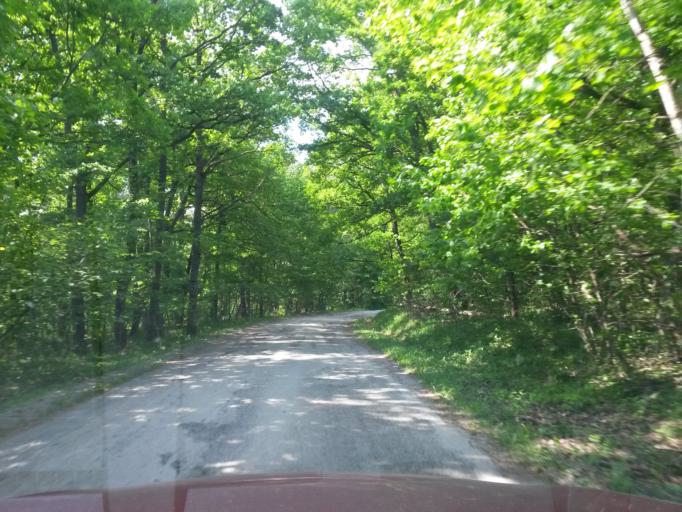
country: SK
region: Kosicky
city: Moldava nad Bodvou
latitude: 48.7127
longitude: 21.0244
